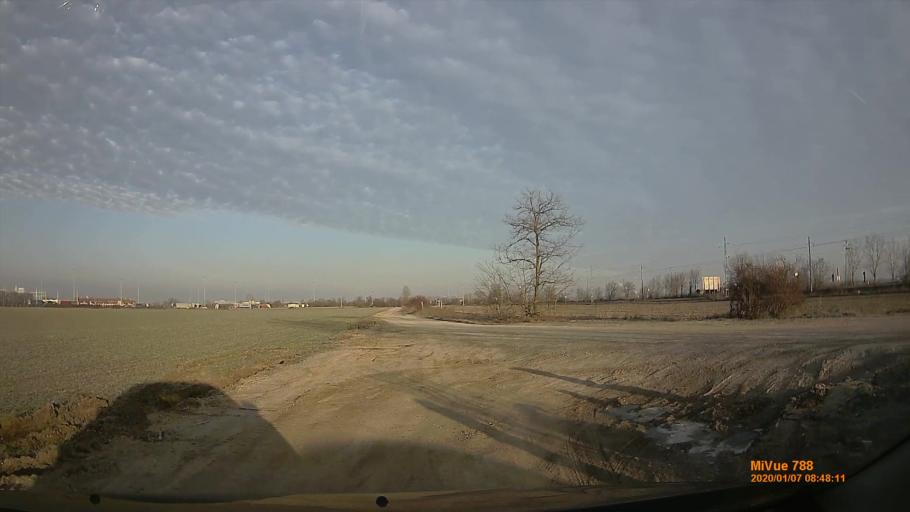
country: HU
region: Gyor-Moson-Sopron
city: Rajka
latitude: 48.0049
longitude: 17.1846
